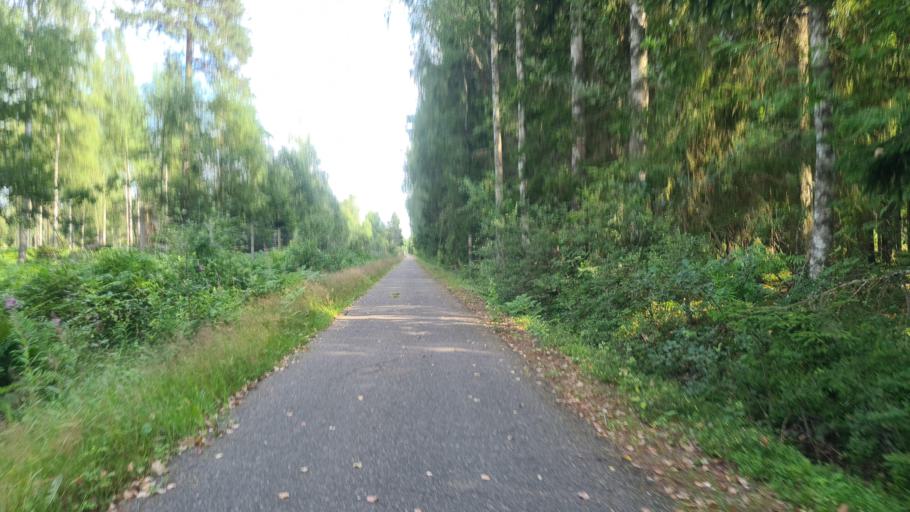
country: SE
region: Joenkoeping
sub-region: Varnamo Kommun
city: Rydaholm
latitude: 56.8593
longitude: 14.1772
